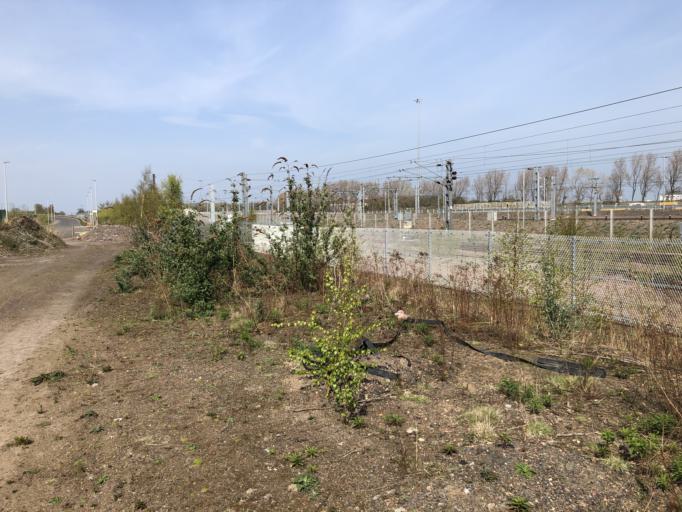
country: GB
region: Scotland
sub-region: Midlothian
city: Dalkeith
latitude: 55.9244
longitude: -3.0835
